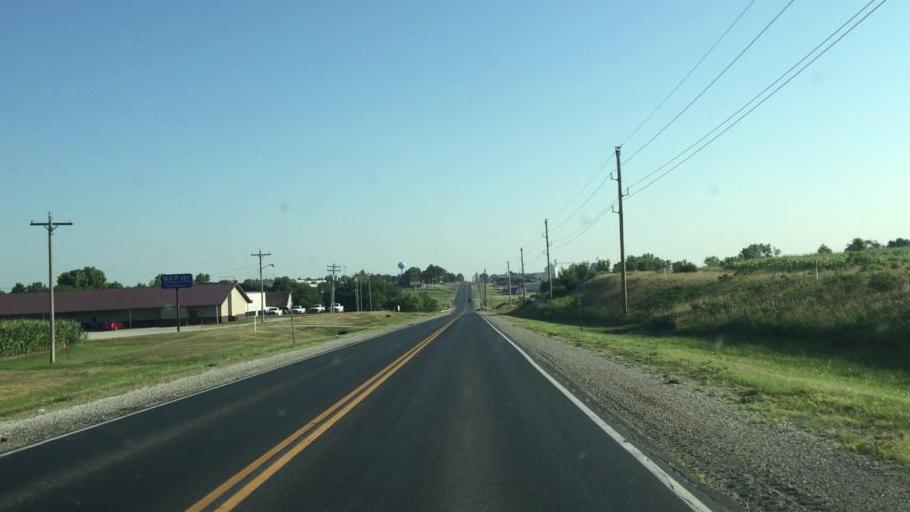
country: US
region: Kansas
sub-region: Nemaha County
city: Sabetha
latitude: 39.8861
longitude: -95.7883
